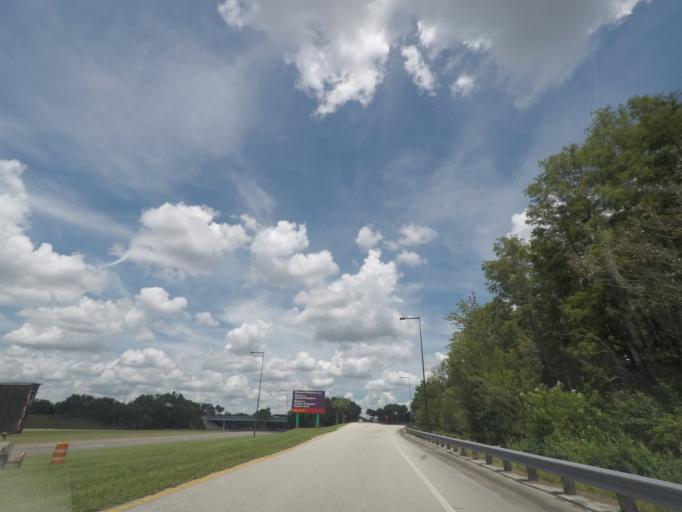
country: US
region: Florida
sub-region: Osceola County
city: Celebration
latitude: 28.3609
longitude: -81.5634
